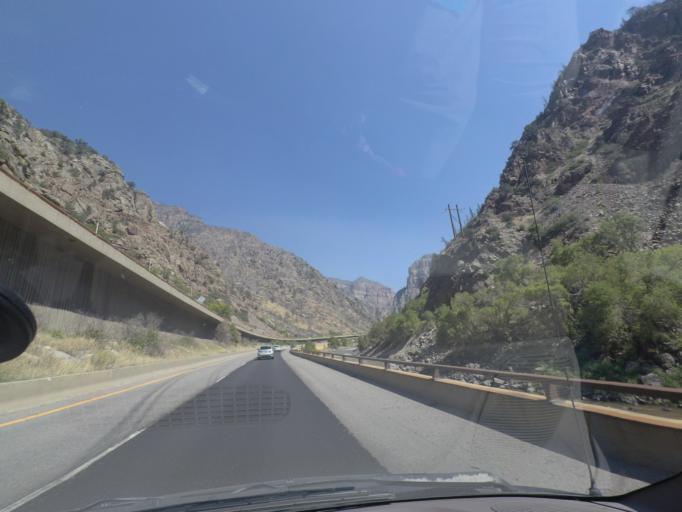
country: US
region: Colorado
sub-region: Garfield County
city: Glenwood Springs
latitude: 39.5625
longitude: -107.2380
